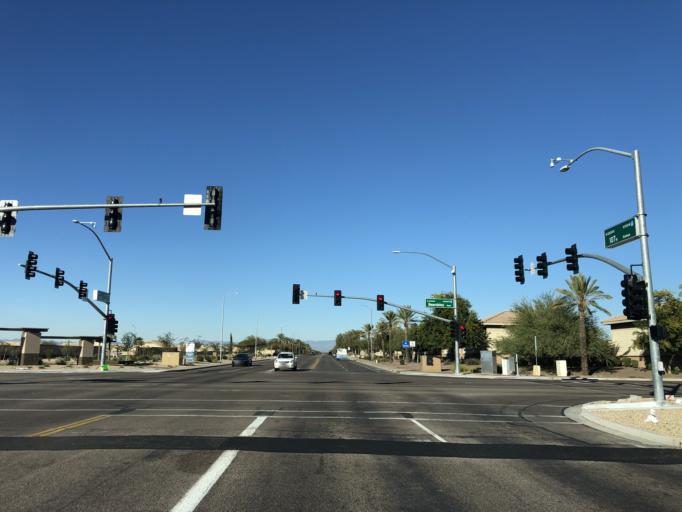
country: US
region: Arizona
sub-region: Maricopa County
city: Sun City West
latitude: 33.6669
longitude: -112.2900
